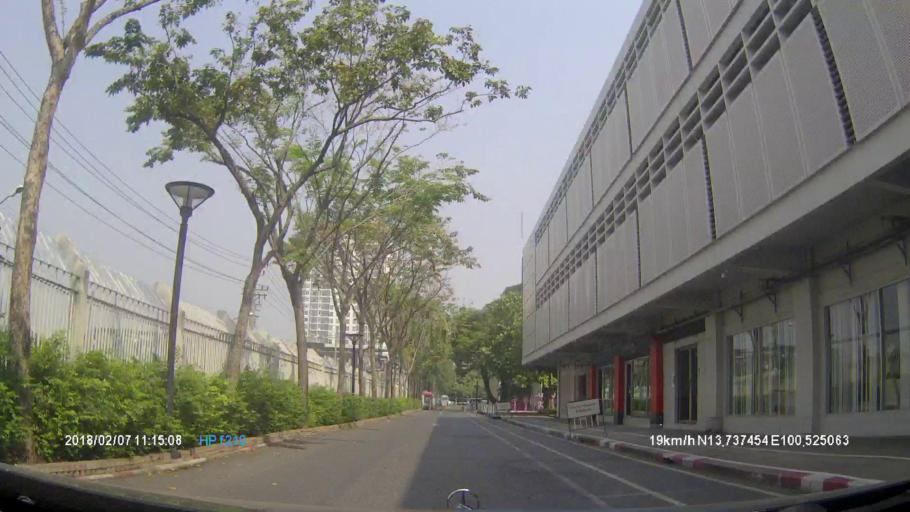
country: TH
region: Bangkok
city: Pathum Wan
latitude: 13.7375
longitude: 100.5251
